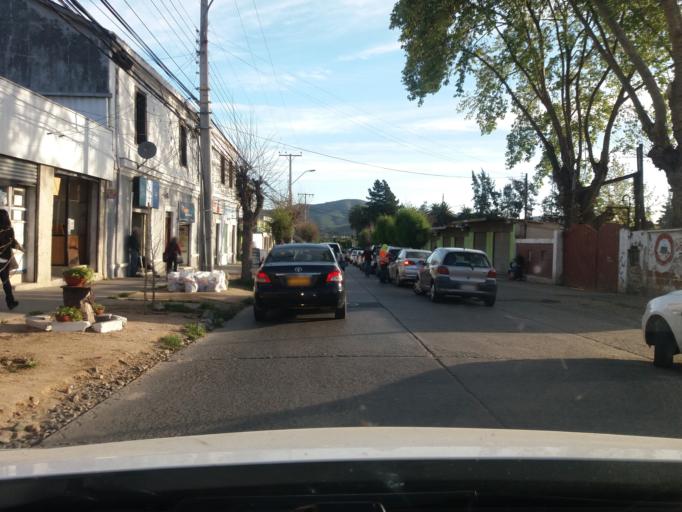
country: CL
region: Valparaiso
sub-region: Provincia de Marga Marga
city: Limache
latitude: -32.9851
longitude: -71.2773
